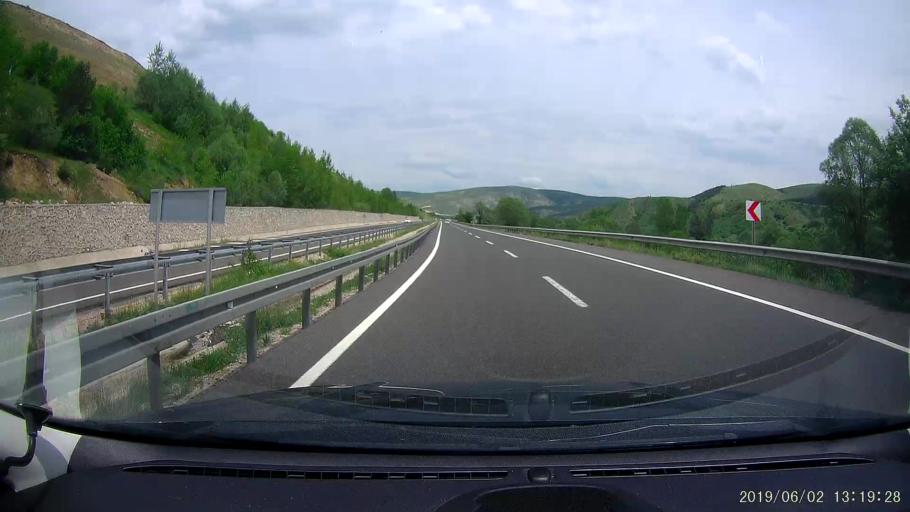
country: TR
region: Cankiri
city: Cerkes
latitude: 40.8326
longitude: 32.7361
